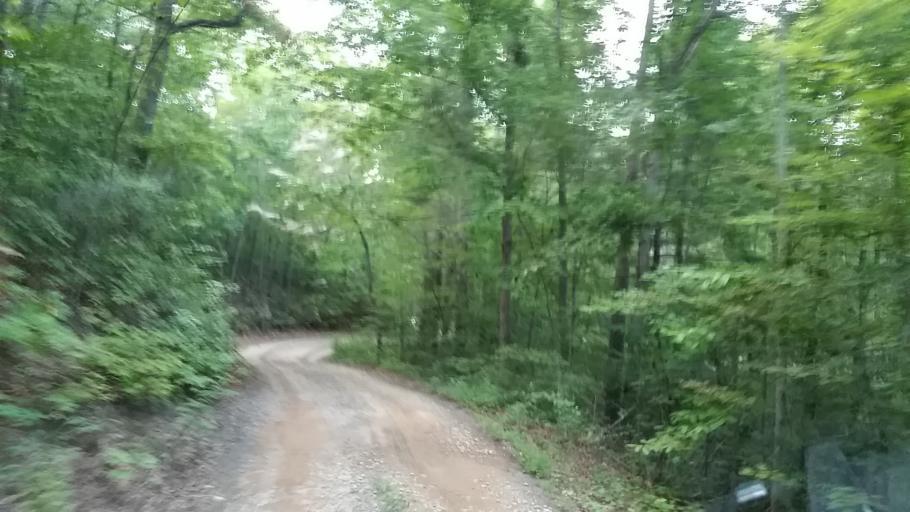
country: US
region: Georgia
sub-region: Lumpkin County
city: Dahlonega
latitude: 34.5970
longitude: -84.0449
